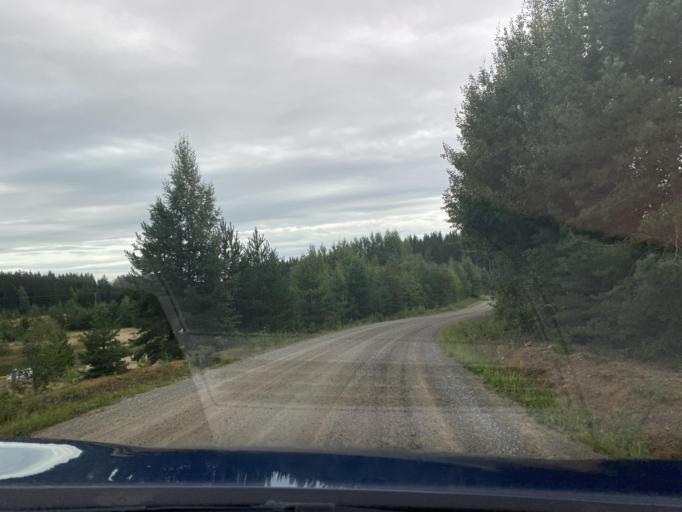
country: FI
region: Pirkanmaa
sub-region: Lounais-Pirkanmaa
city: Punkalaidun
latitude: 61.2461
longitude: 23.0453
